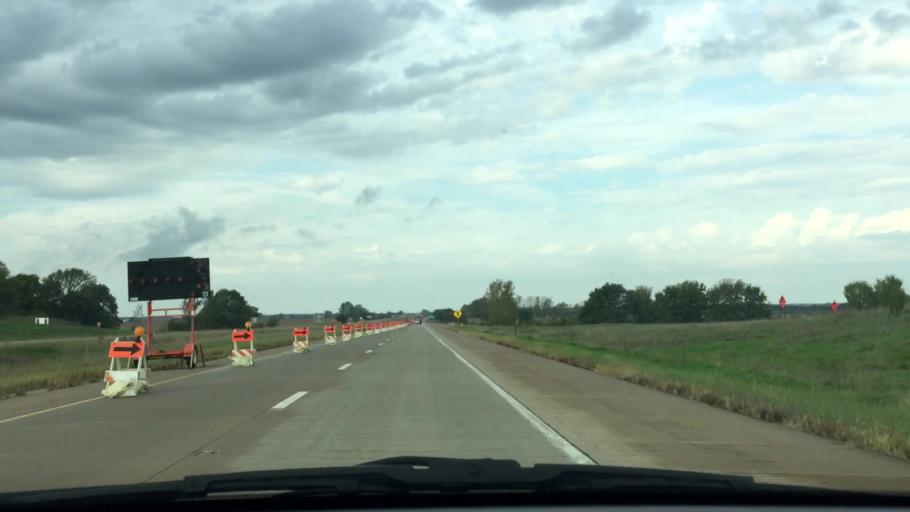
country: US
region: Illinois
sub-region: Whiteside County
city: Prophetstown
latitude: 41.7222
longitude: -89.9685
